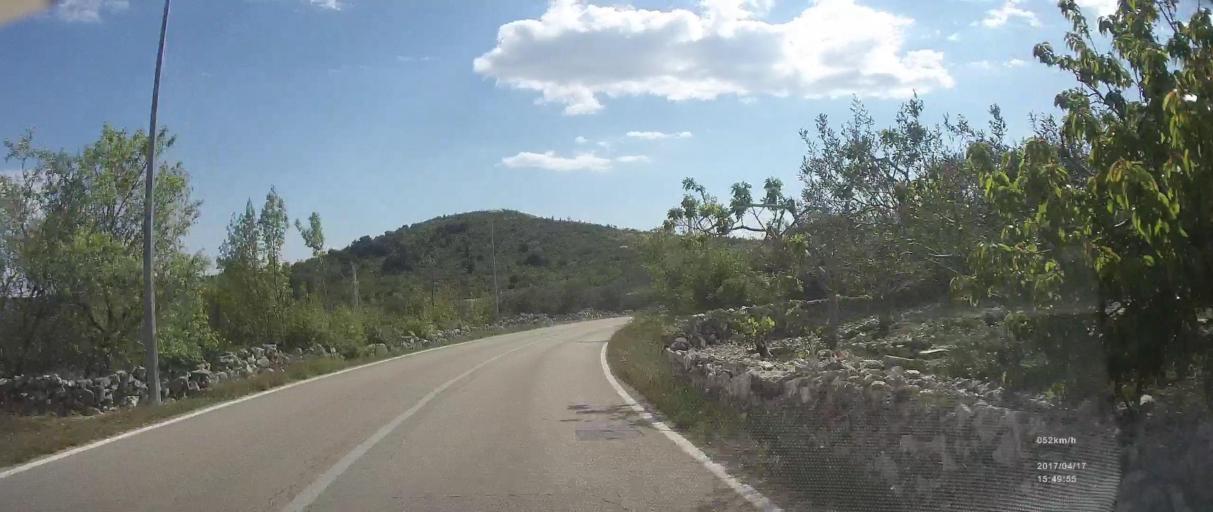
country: HR
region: Sibensko-Kniniska
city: Primosten
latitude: 43.6104
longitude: 15.9765
